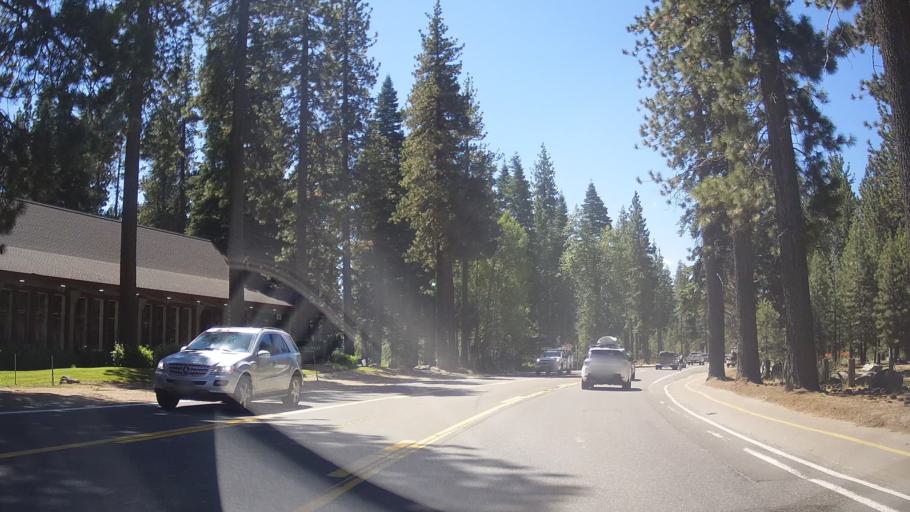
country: US
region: California
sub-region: Placer County
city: Sunnyside-Tahoe City
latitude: 39.1661
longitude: -120.1440
